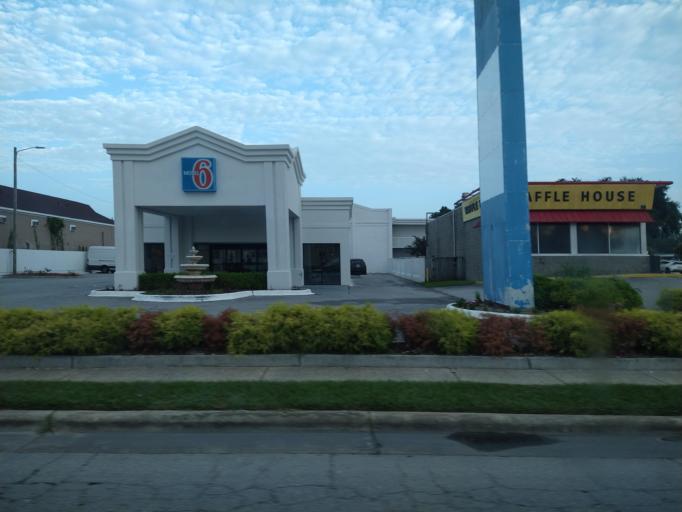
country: US
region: North Carolina
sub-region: Onslow County
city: Jacksonville
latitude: 34.7605
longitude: -77.4159
